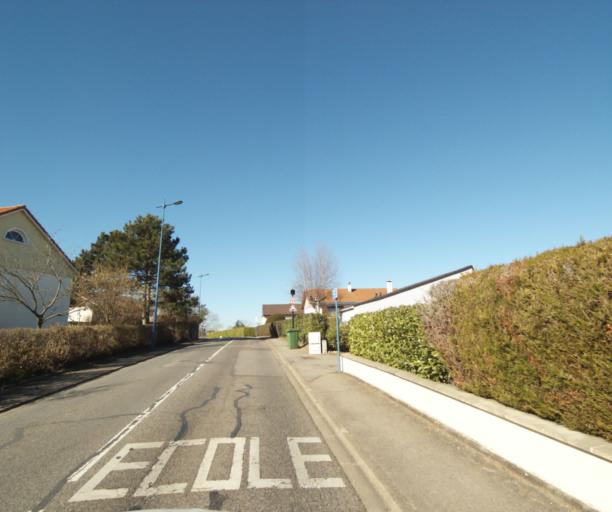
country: FR
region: Lorraine
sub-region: Departement de Meurthe-et-Moselle
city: Heillecourt
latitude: 48.6445
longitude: 6.1989
